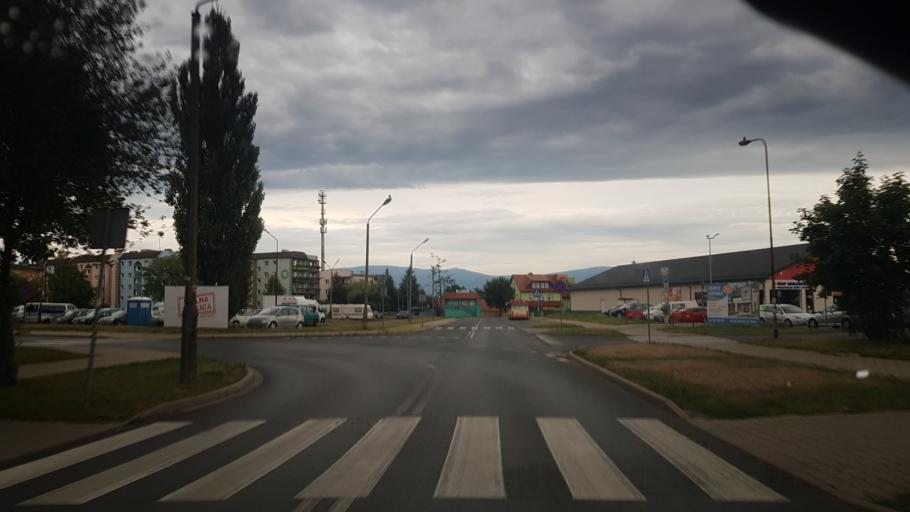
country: PL
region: Lower Silesian Voivodeship
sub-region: Powiat jeleniogorski
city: Jezow Sudecki
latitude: 50.9194
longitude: 15.7494
